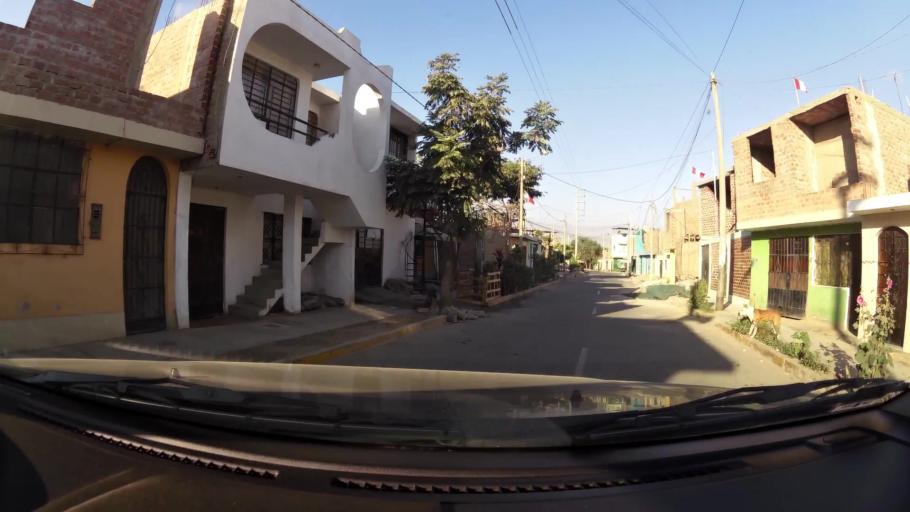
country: PE
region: Ica
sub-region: Provincia de Ica
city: Ica
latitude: -14.0671
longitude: -75.7209
